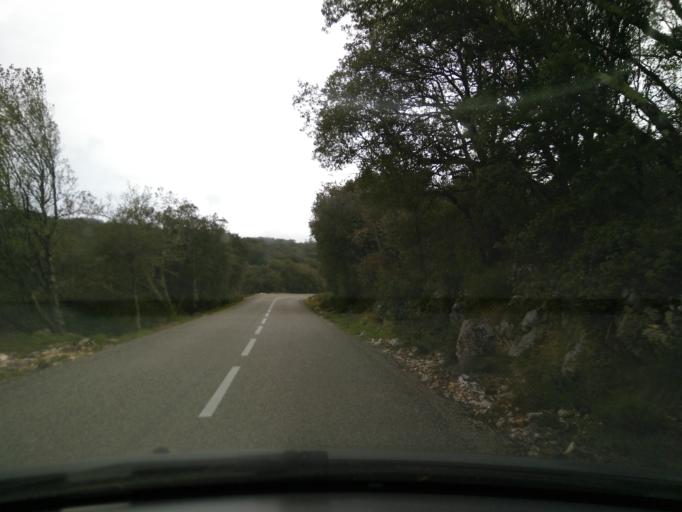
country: FR
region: Languedoc-Roussillon
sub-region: Departement du Gard
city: Barjac
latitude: 44.3216
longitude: 4.4243
